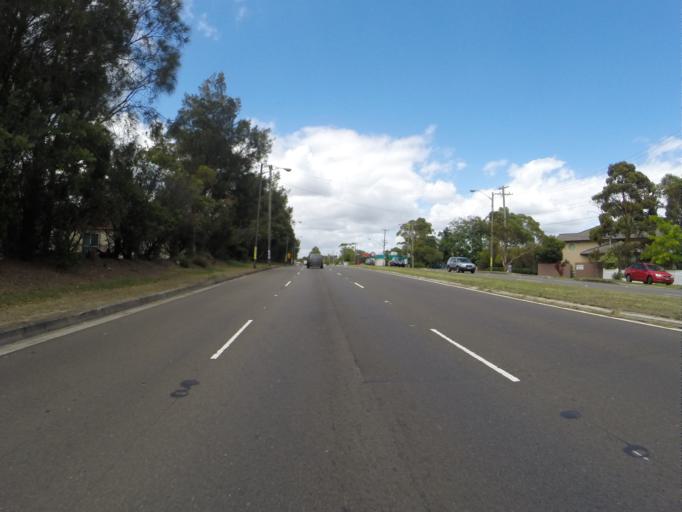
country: AU
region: New South Wales
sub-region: Sutherland Shire
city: Heathcote
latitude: -34.0895
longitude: 151.0055
